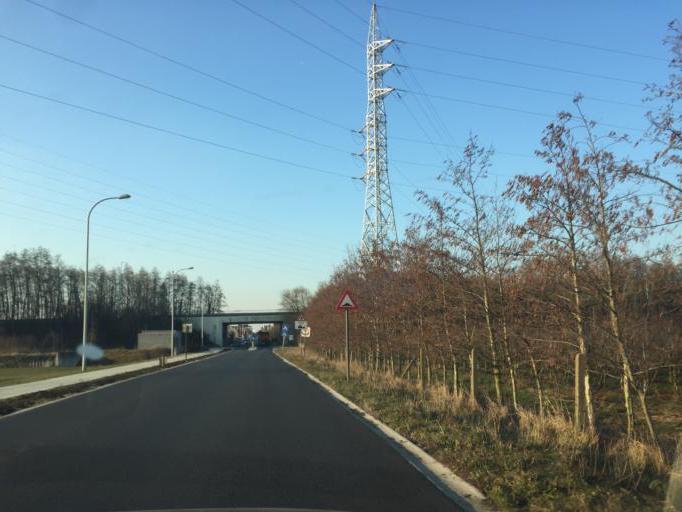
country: BE
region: Flanders
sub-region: Provincie West-Vlaanderen
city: Pittem
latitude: 50.9857
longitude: 3.2667
